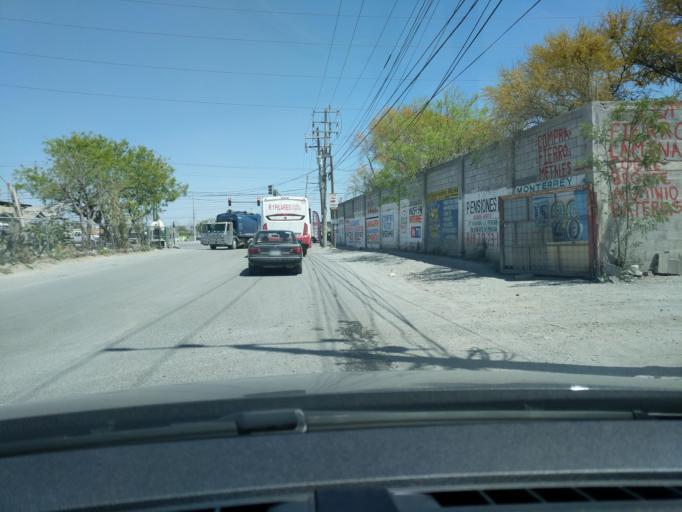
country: MX
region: Nuevo Leon
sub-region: Salinas Victoria
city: Emiliano Zapata
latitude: 25.9104
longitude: -100.2676
